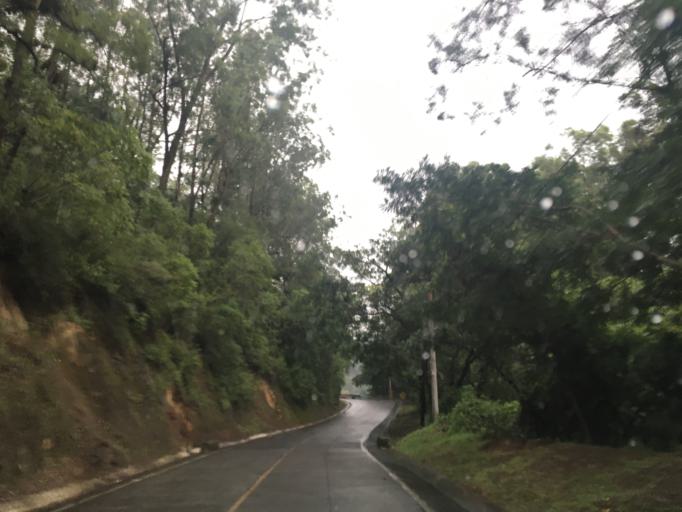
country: GT
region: Sacatepequez
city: Antigua Guatemala
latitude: 14.5672
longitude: -90.7273
